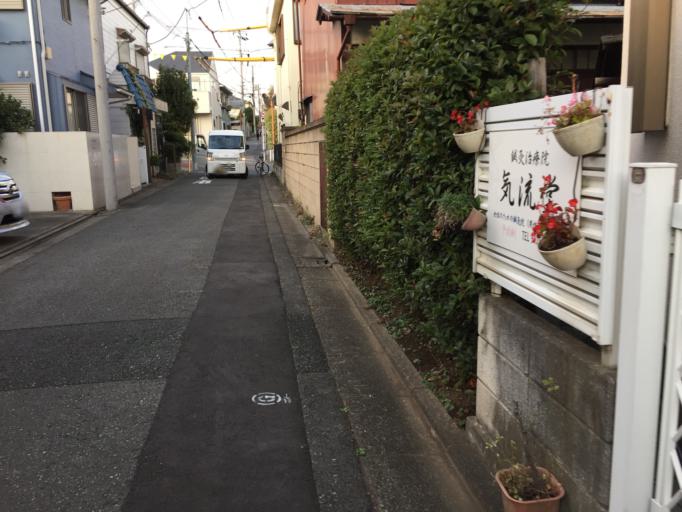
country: JP
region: Tokyo
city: Tokyo
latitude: 35.6476
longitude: 139.6452
